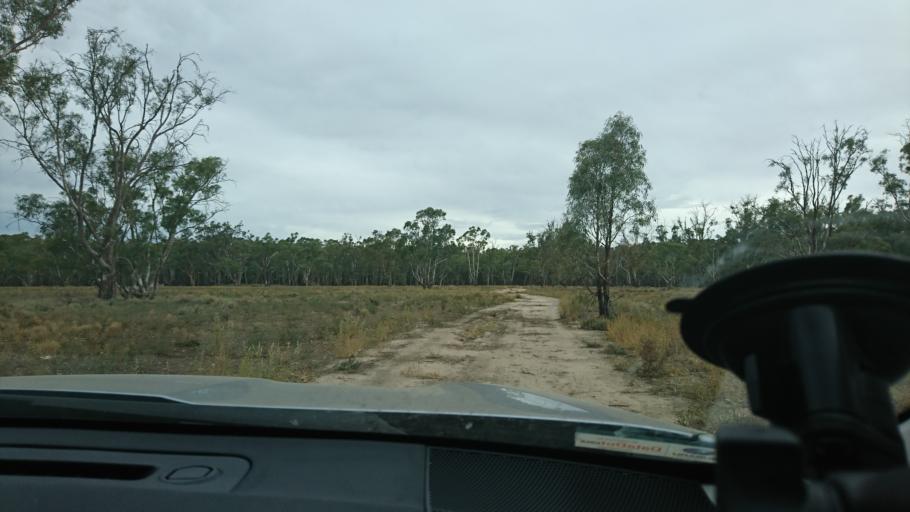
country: AU
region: Victoria
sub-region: Swan Hill
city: Swan Hill
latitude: -35.1402
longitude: 143.3801
